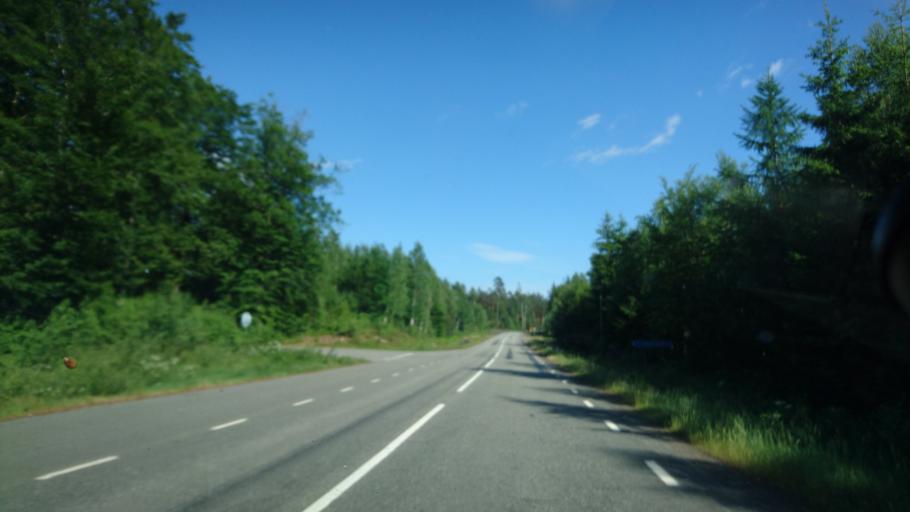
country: SE
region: Skane
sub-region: Osby Kommun
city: Lonsboda
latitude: 56.4316
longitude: 14.2627
